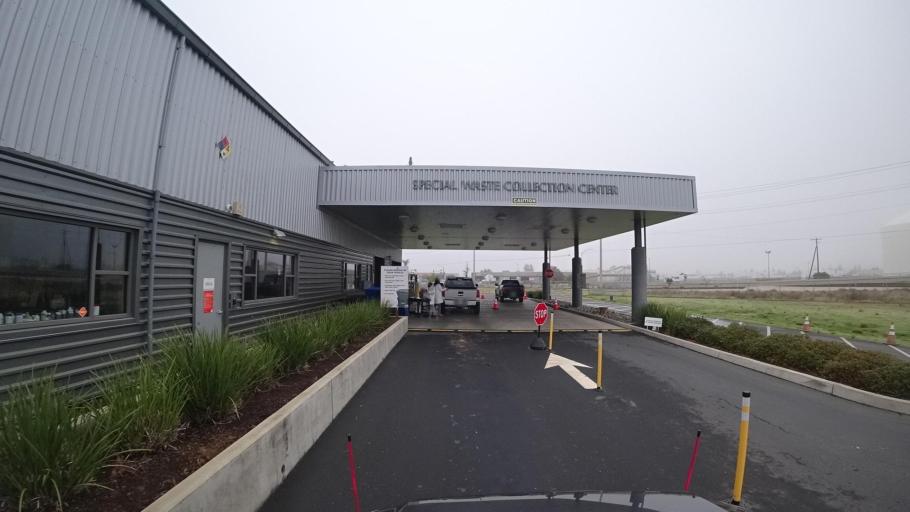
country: US
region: California
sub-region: Sacramento County
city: Elk Grove
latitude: 38.3789
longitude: -121.3561
